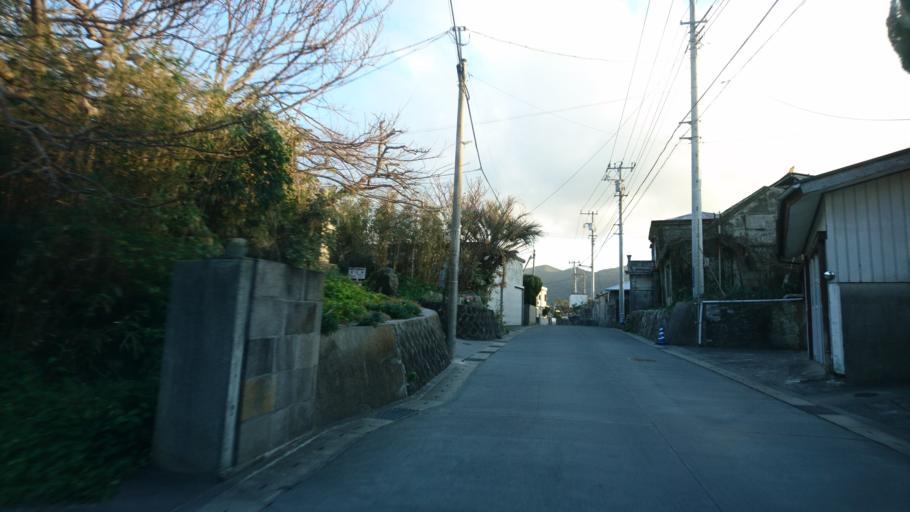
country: JP
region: Shizuoka
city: Shimoda
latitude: 34.3751
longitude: 139.2575
